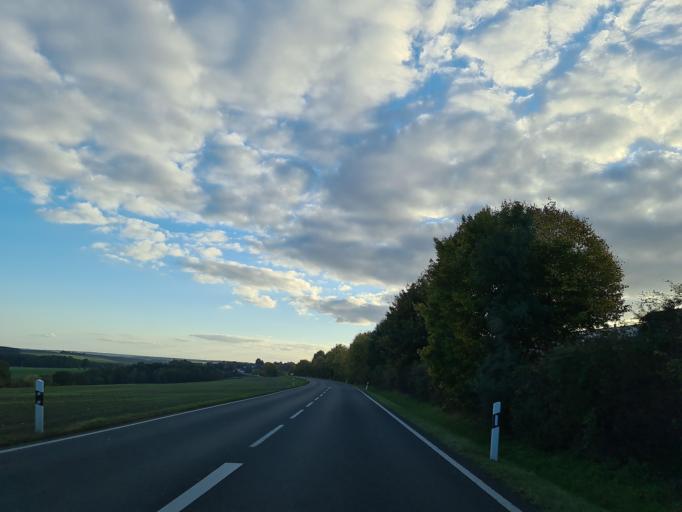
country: DE
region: Thuringia
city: Teichwitz
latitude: 50.7497
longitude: 12.0908
